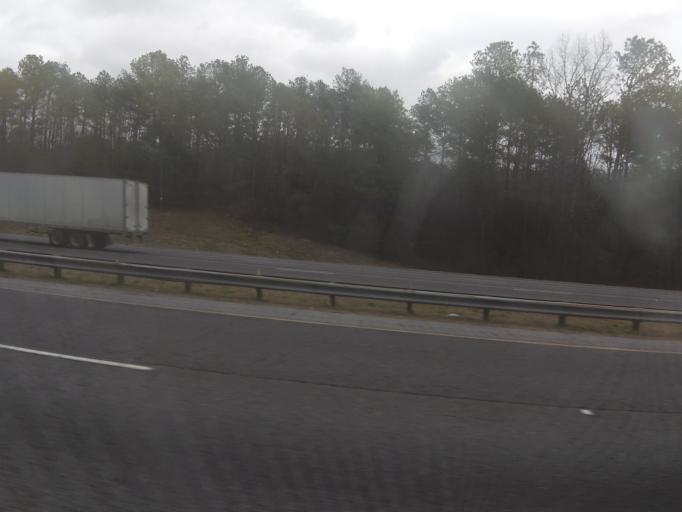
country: US
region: Georgia
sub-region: Gordon County
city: Calhoun
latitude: 34.6027
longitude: -84.9576
